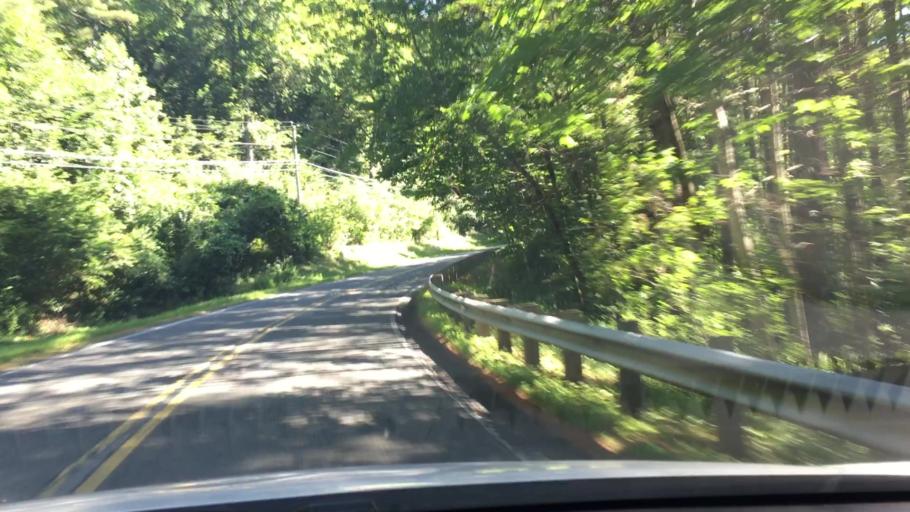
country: US
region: Massachusetts
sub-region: Berkshire County
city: West Stockbridge
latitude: 42.3059
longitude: -73.3719
